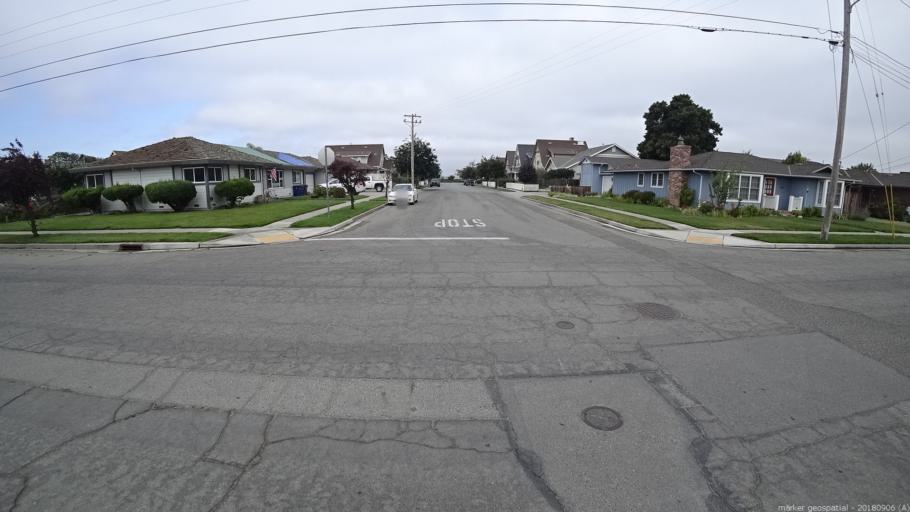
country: US
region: California
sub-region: Monterey County
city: Salinas
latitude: 36.6247
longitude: -121.6482
